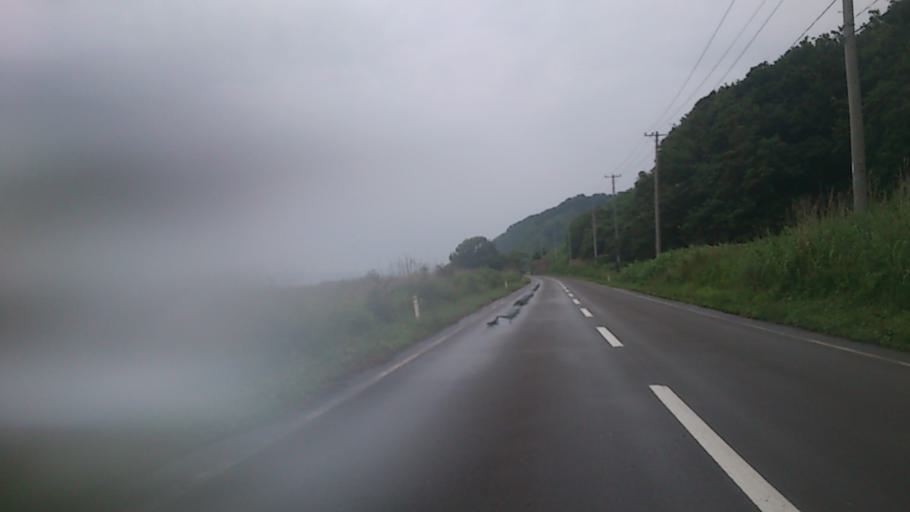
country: JP
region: Akita
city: Noshiromachi
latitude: 40.4711
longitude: 139.9469
